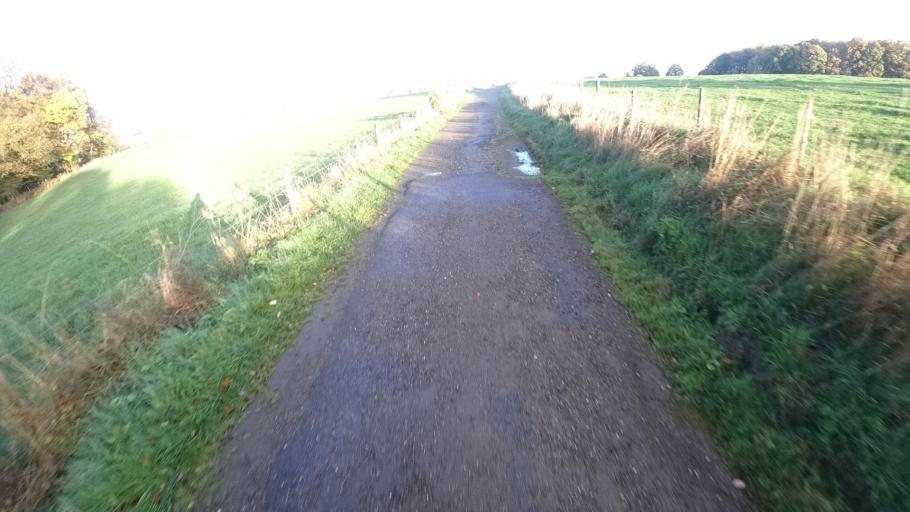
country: DE
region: Rheinland-Pfalz
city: Berg
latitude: 50.5578
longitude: 6.9678
